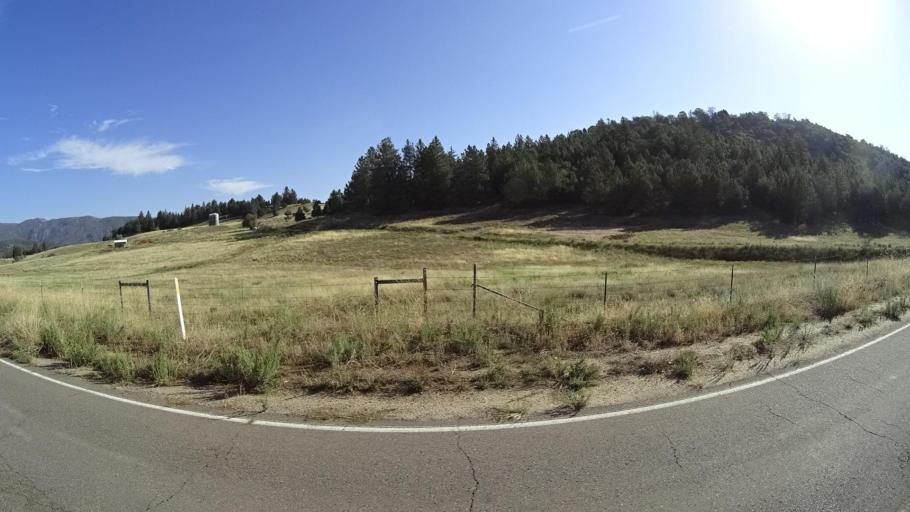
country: US
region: California
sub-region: Riverside County
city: Aguanga
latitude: 33.2820
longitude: -116.7882
